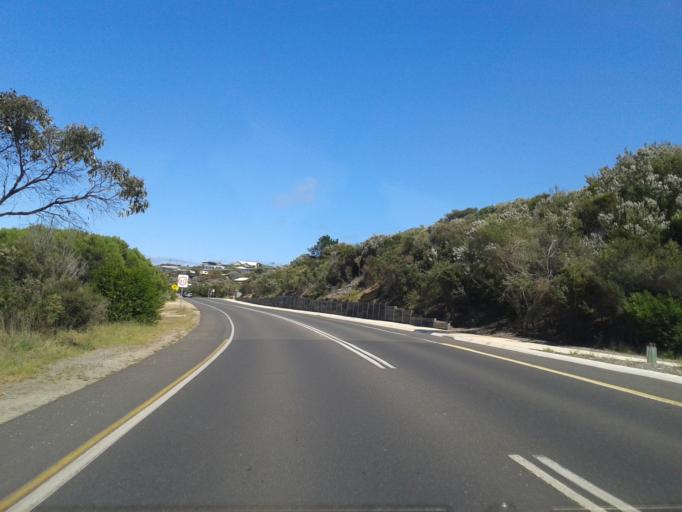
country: AU
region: Victoria
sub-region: Surf Coast
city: Anglesea
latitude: -38.4649
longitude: 144.0938
